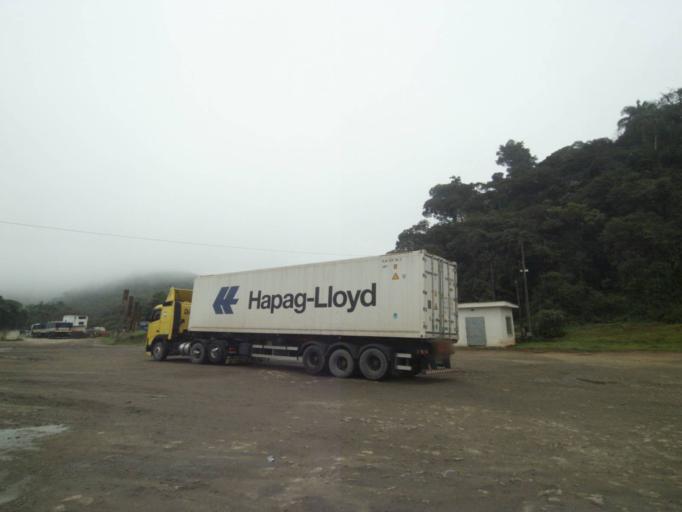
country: BR
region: Parana
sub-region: Paranagua
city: Paranagua
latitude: -25.5616
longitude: -48.5919
